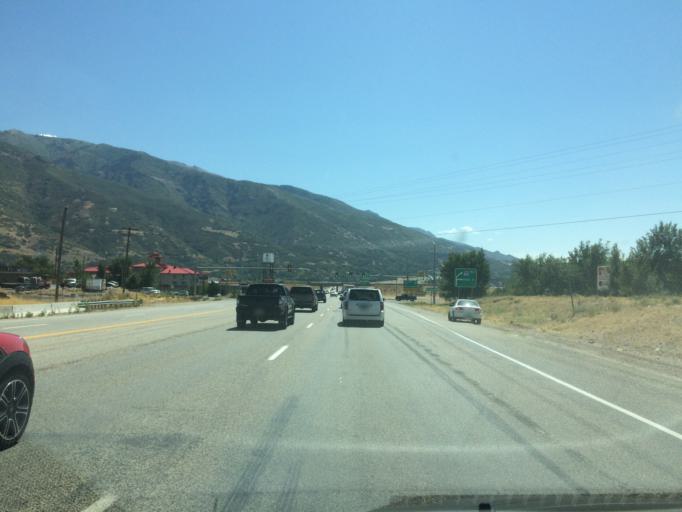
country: US
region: Utah
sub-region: Weber County
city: Uintah
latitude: 41.1413
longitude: -111.9167
